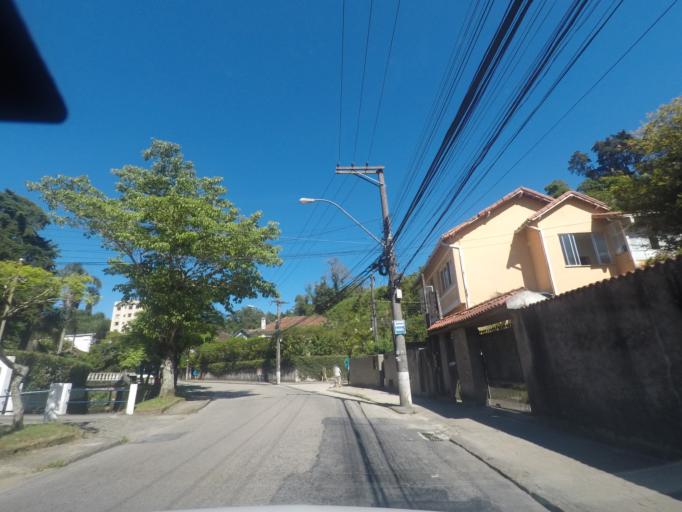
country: BR
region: Rio de Janeiro
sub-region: Petropolis
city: Petropolis
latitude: -22.5211
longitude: -43.1869
